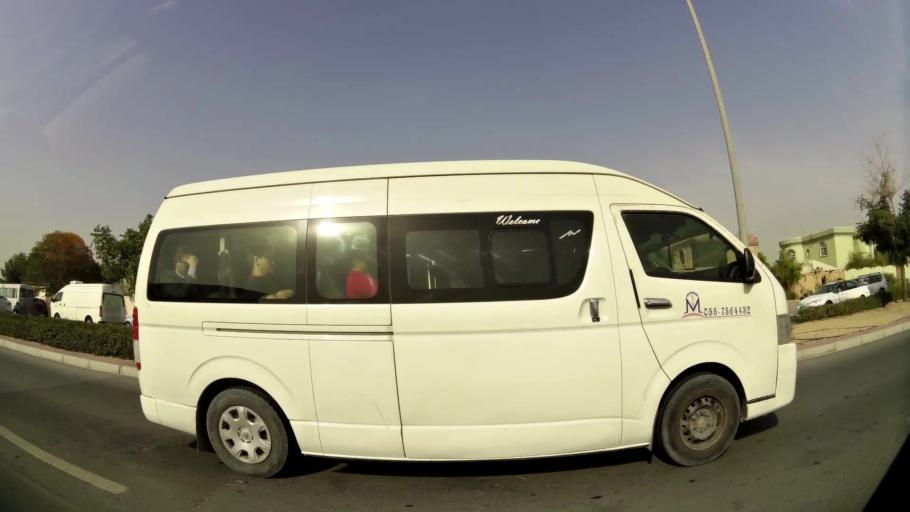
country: AE
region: Ash Shariqah
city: Sharjah
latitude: 25.2537
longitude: 55.4301
